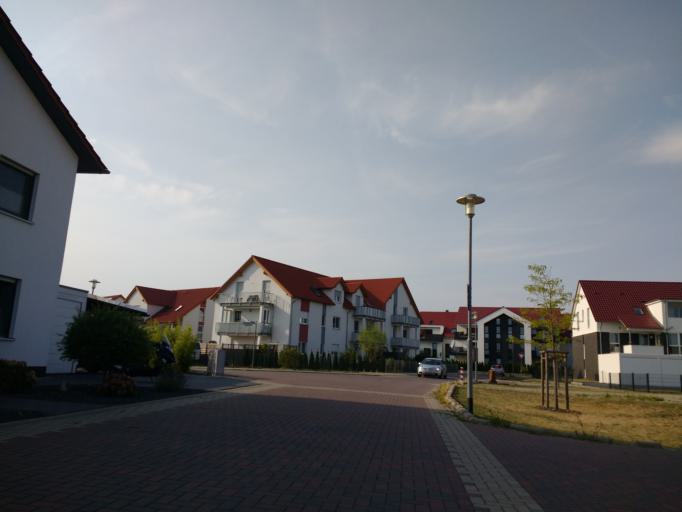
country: DE
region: Lower Saxony
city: Gifhorn
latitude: 52.4965
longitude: 10.5343
